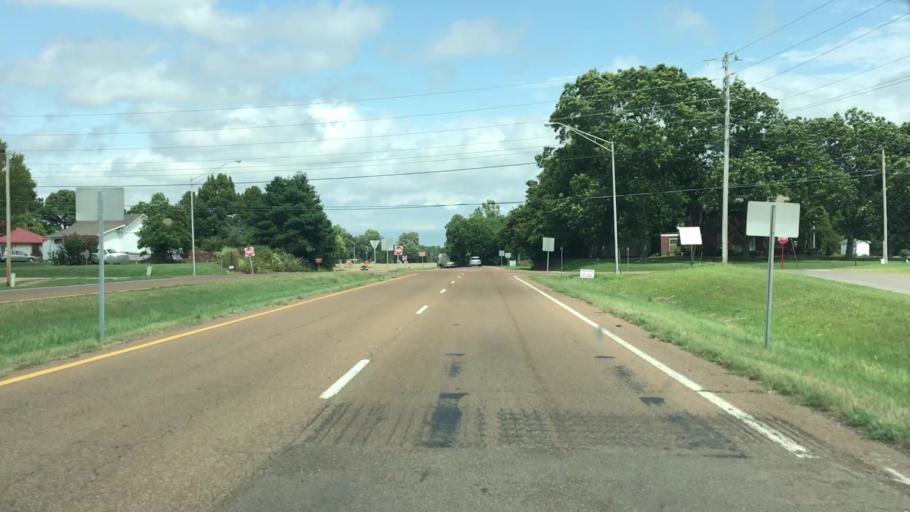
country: US
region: Tennessee
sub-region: Obion County
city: Troy
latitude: 36.3353
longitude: -89.1603
